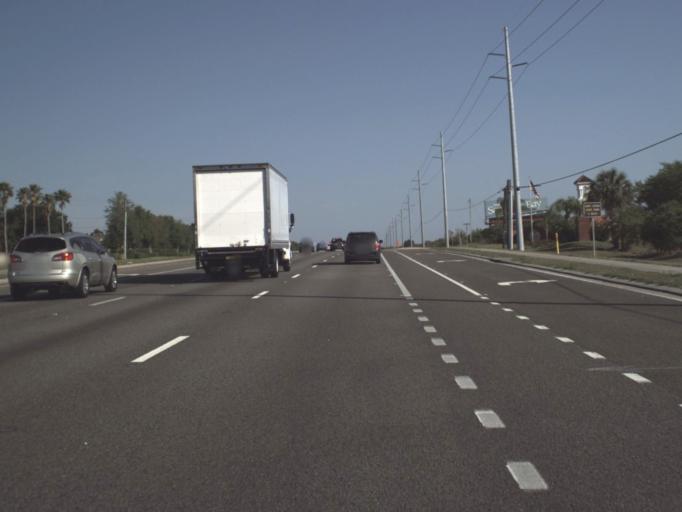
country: US
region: Florida
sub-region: Lake County
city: Four Corners
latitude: 28.3872
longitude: -81.6905
